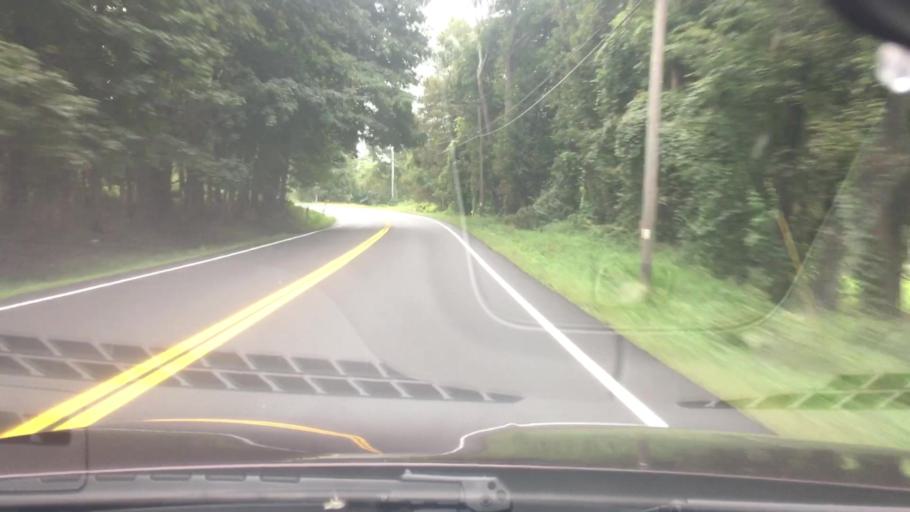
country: US
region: New York
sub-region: Dutchess County
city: Millbrook
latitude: 41.8156
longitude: -73.6304
